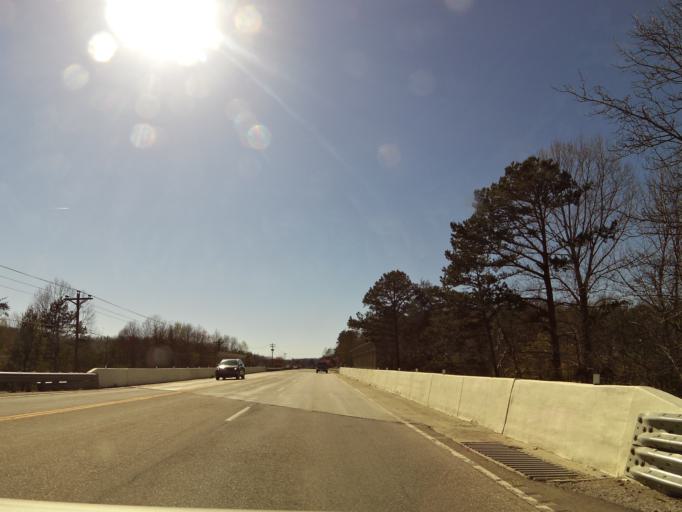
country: US
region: Tennessee
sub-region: Scott County
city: Oneida
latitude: 36.5383
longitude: -84.4639
